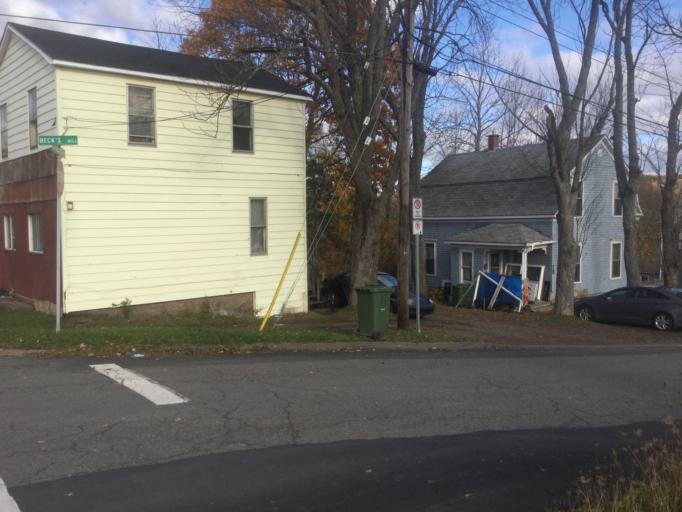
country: CA
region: Nova Scotia
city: New Glasgow
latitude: 45.5868
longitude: -62.6520
